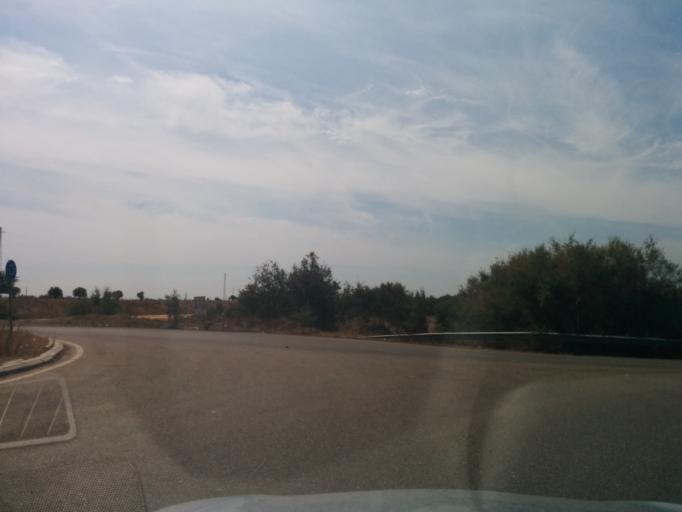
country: ES
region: Andalusia
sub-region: Provincia de Sevilla
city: Gelves
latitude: 37.3219
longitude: -5.9856
